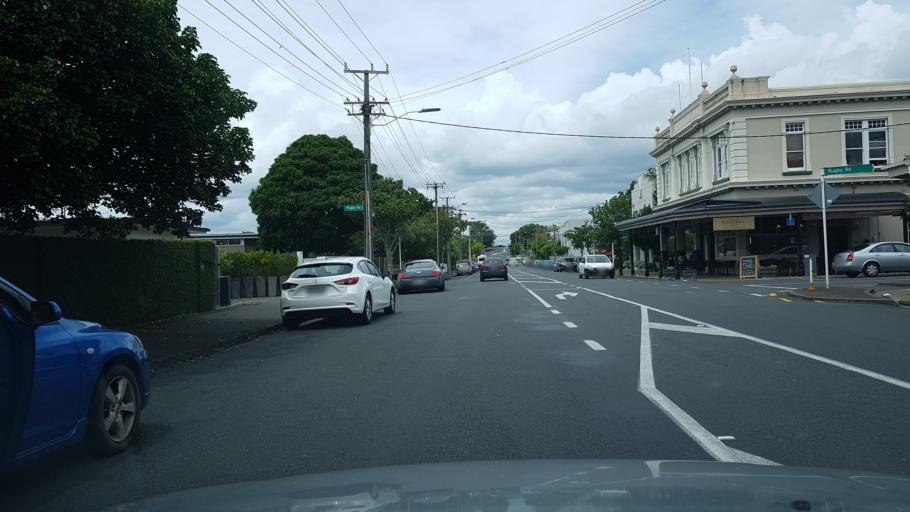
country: NZ
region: Auckland
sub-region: Auckland
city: North Shore
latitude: -36.8166
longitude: 174.7322
